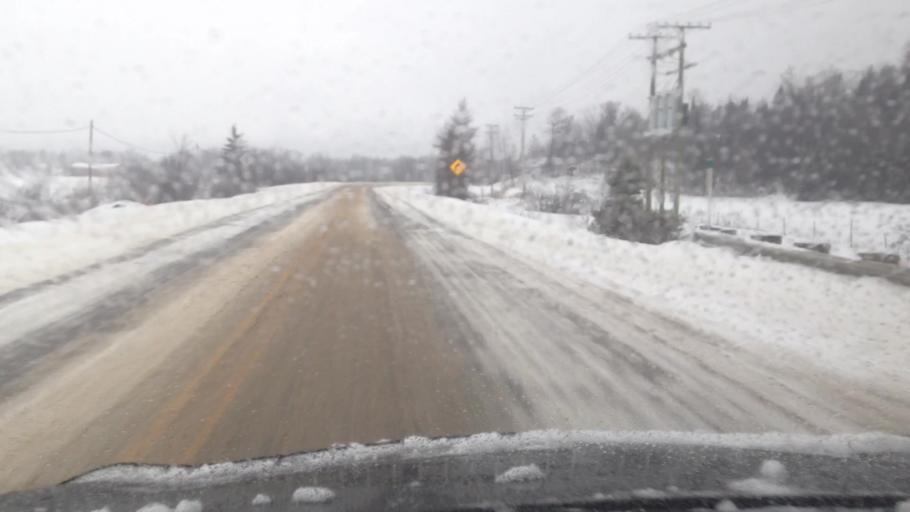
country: CA
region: Quebec
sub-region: Laurentides
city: Mont-Tremblant
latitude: 46.0692
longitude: -74.6212
